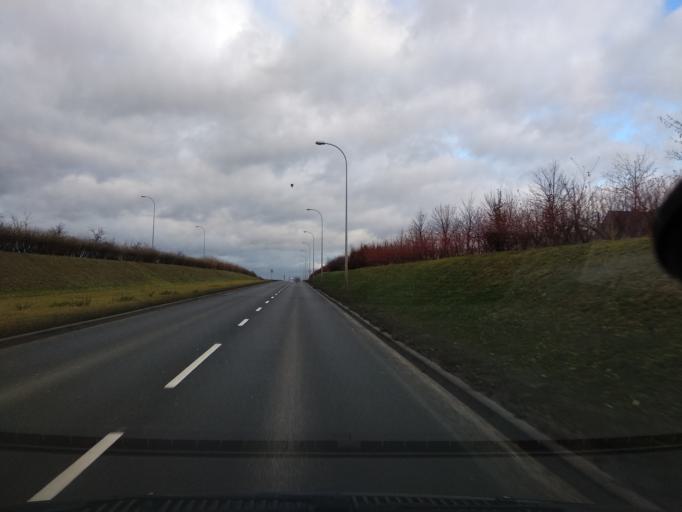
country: PL
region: Greater Poland Voivodeship
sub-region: Kalisz
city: Kalisz
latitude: 51.7800
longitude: 18.0816
